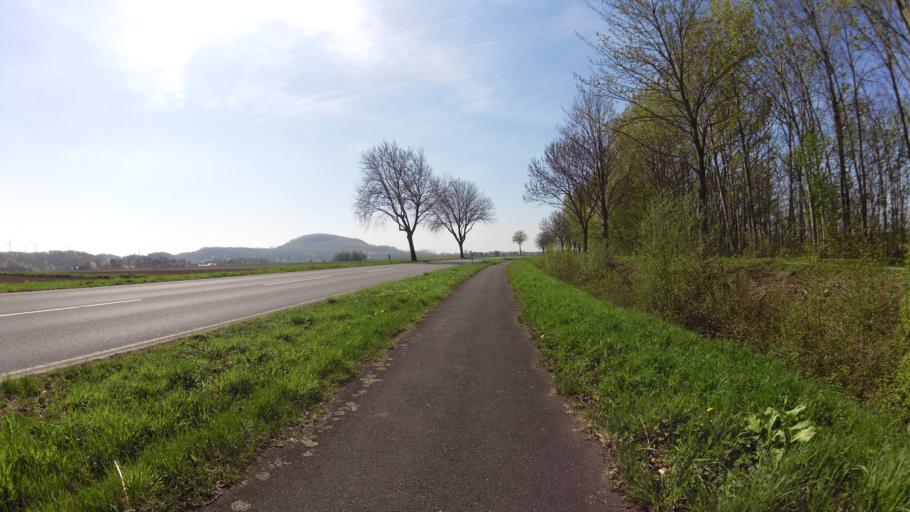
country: DE
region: North Rhine-Westphalia
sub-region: Regierungsbezirk Koln
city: Ubach-Palenberg
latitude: 50.9112
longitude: 6.1020
